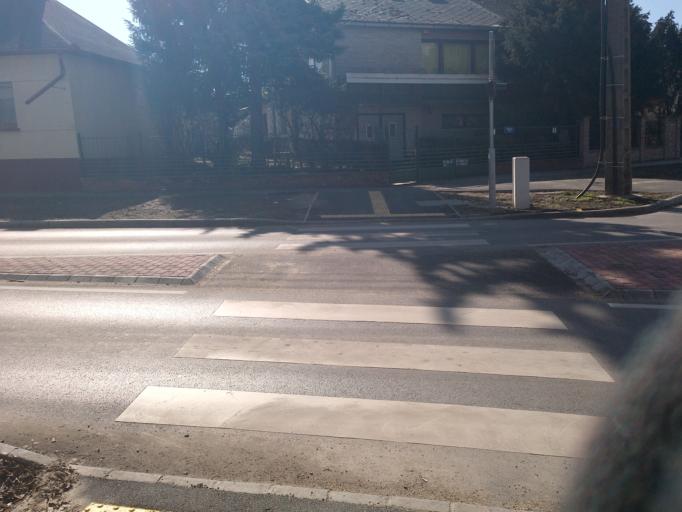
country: HU
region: Hajdu-Bihar
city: Hajduszoboszlo
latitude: 47.4408
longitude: 21.3967
